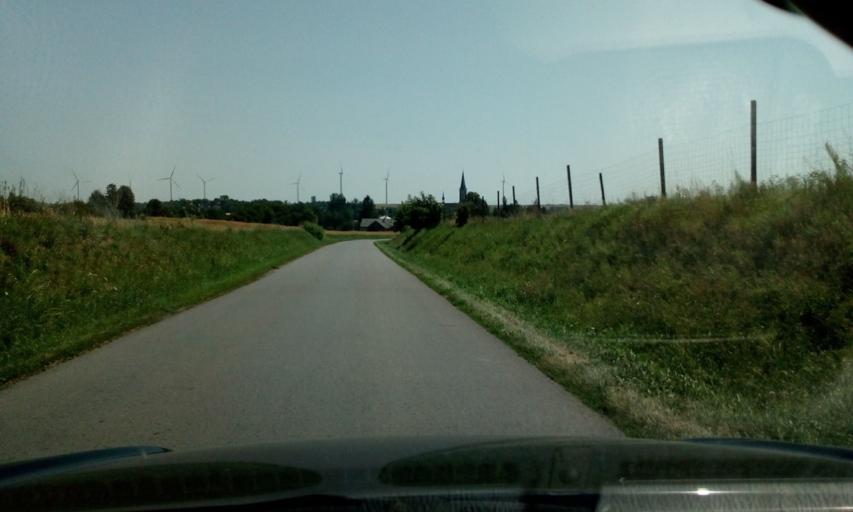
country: PL
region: Subcarpathian Voivodeship
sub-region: Powiat lancucki
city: Wysoka
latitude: 50.0474
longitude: 22.2428
